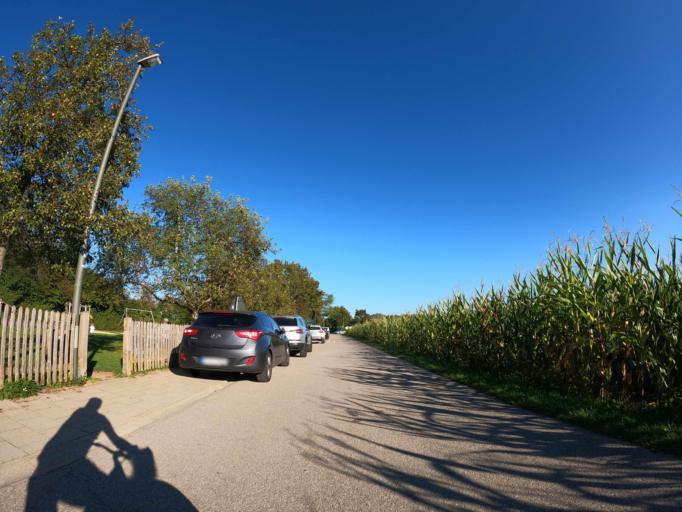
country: DE
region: Bavaria
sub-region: Upper Bavaria
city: Grasbrunn
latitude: 48.0564
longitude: 11.7782
